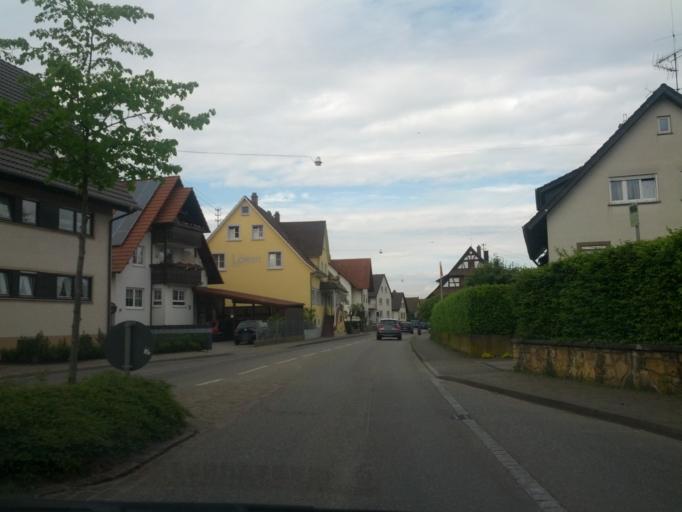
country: DE
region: Baden-Wuerttemberg
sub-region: Freiburg Region
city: Umkirch
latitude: 48.0698
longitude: 7.7988
